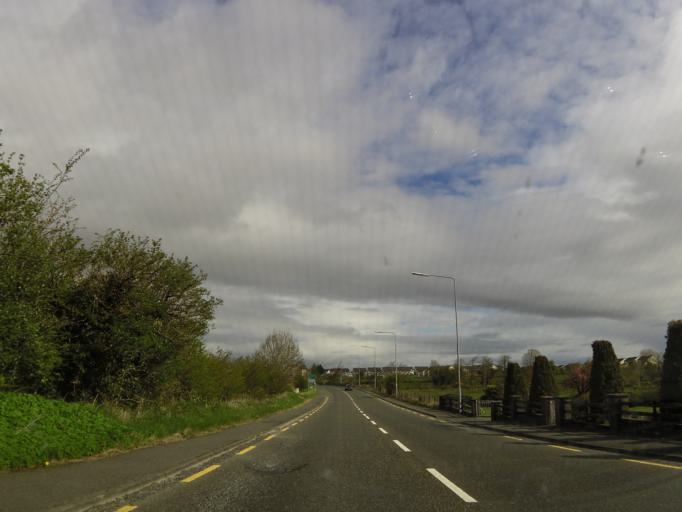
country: IE
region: Connaught
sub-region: Sligo
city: Tobercurry
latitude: 53.9580
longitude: -8.7932
